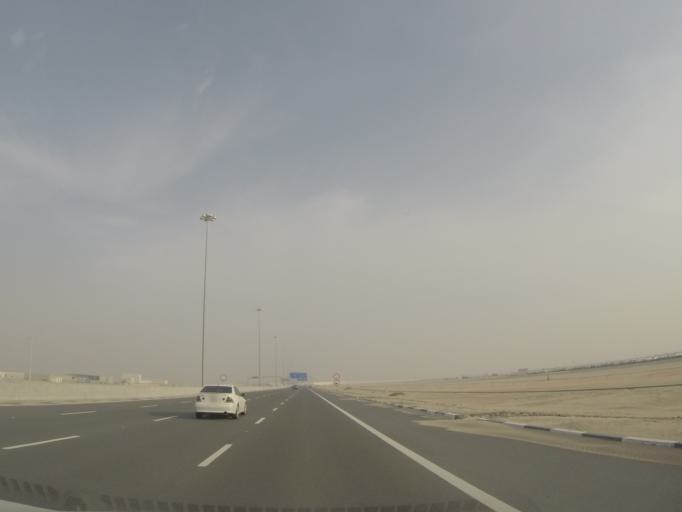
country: AE
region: Abu Dhabi
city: Abu Dhabi
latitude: 24.7531
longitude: 54.7347
